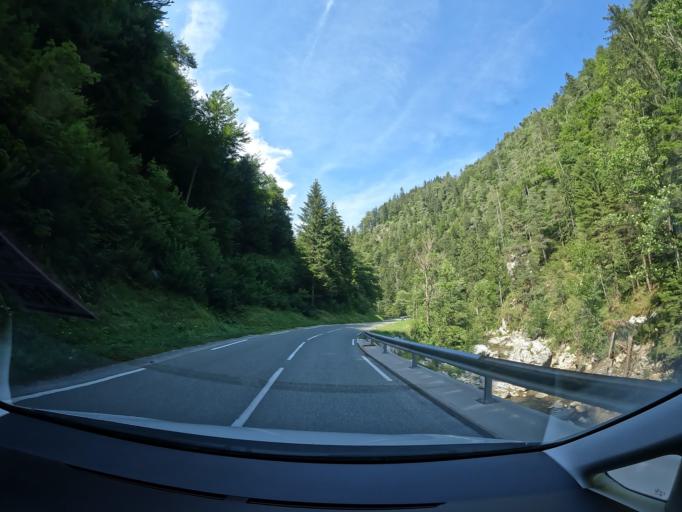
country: SI
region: Trzic
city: Bistrica pri Trzicu
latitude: 46.4301
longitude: 14.2419
